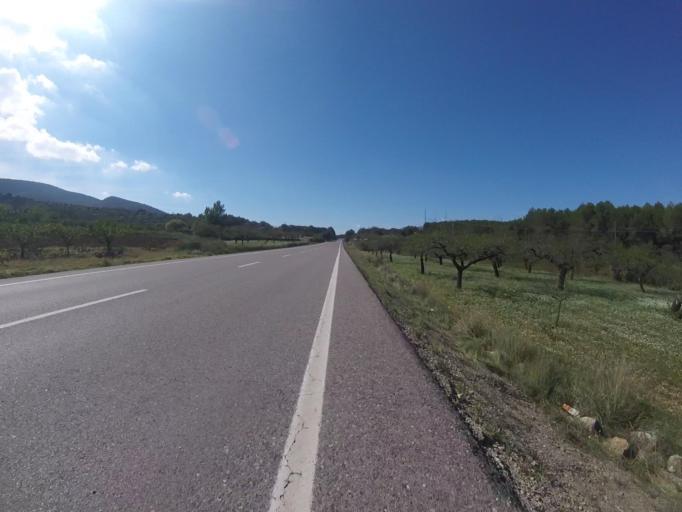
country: ES
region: Valencia
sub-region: Provincia de Castello
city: Sarratella
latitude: 40.3246
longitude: -0.0213
